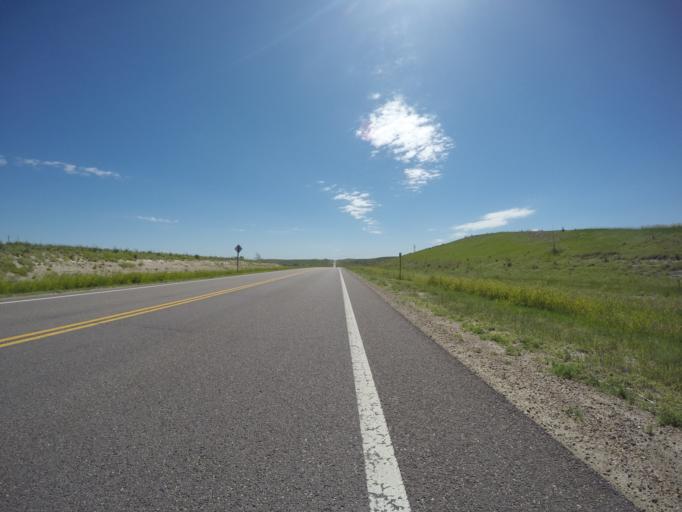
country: US
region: Kansas
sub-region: Rawlins County
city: Atwood
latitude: 39.8133
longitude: -101.0215
